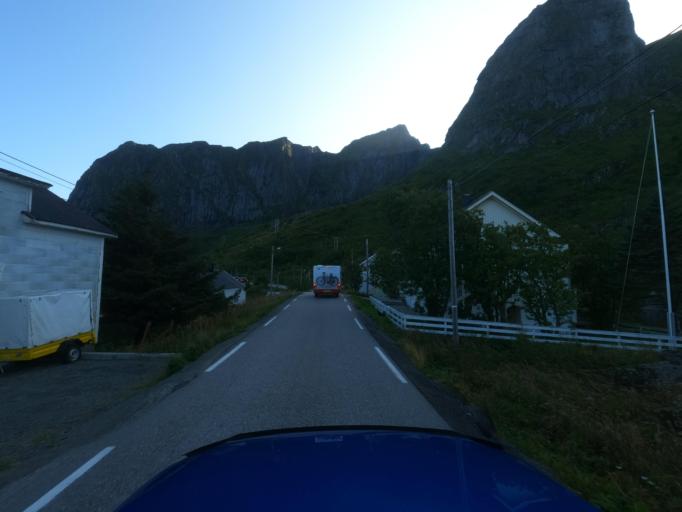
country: NO
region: Nordland
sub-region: Moskenes
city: Reine
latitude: 67.9383
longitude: 13.0732
